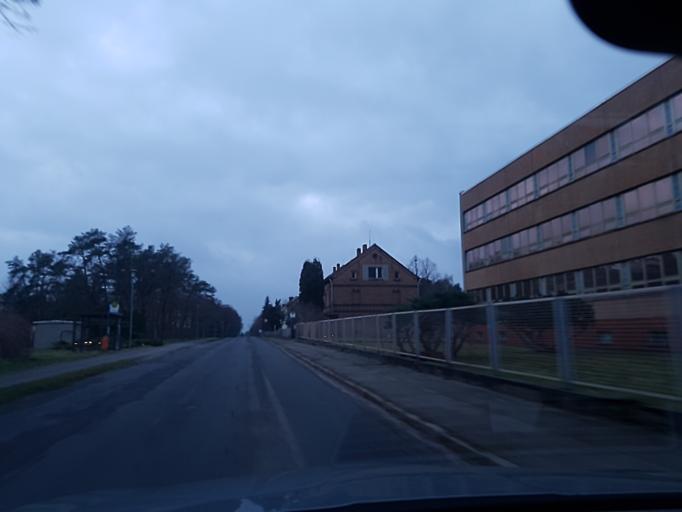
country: DE
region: Brandenburg
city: Schonborn
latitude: 51.6010
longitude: 13.4782
